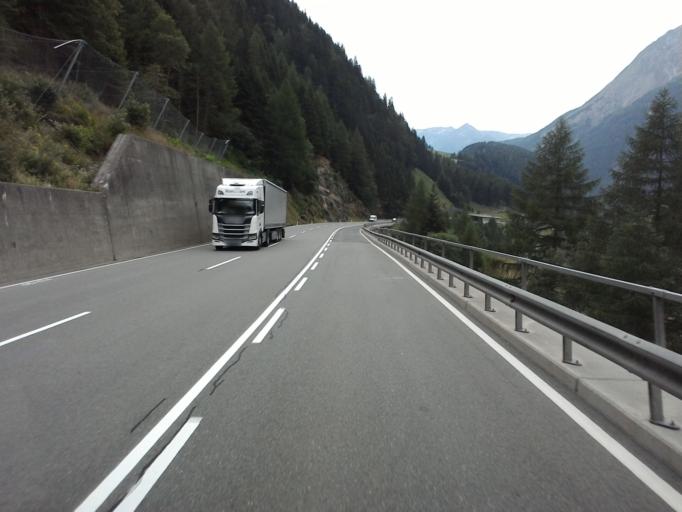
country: AT
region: Tyrol
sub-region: Politischer Bezirk Lienz
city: Matrei in Osttirol
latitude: 47.0691
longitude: 12.5320
